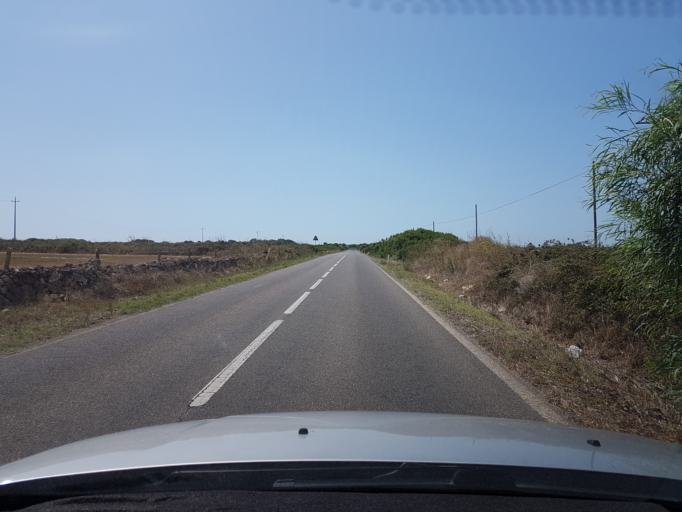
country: IT
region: Sardinia
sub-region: Provincia di Oristano
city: Riola Sardo
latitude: 40.0223
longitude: 8.4705
